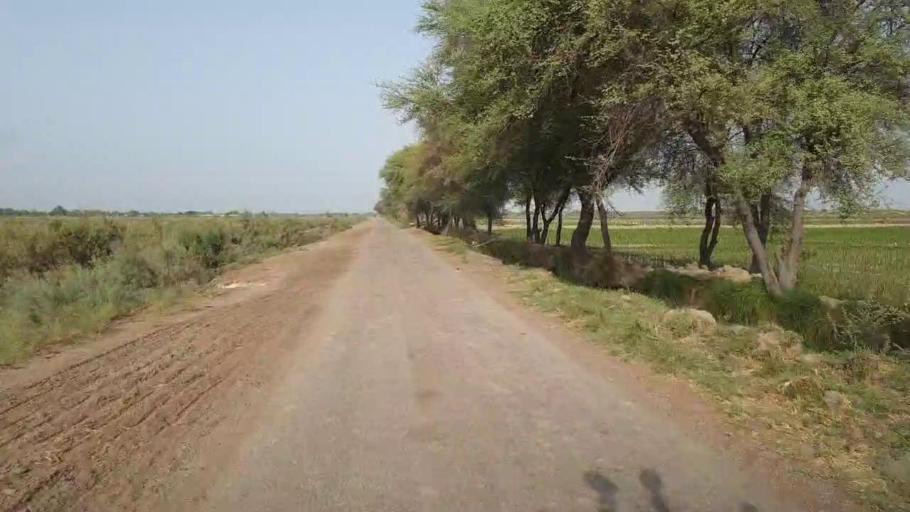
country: PK
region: Sindh
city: Daur
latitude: 26.3401
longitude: 68.2288
